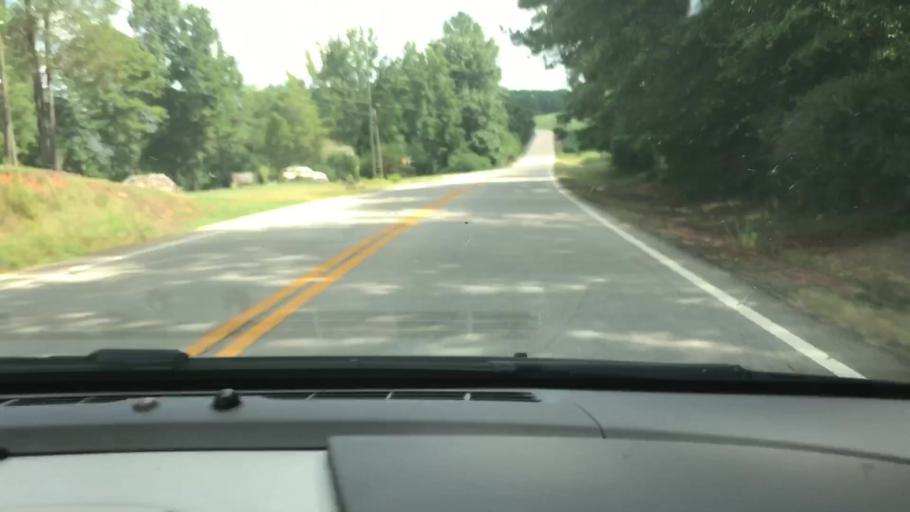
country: US
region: Georgia
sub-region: Troup County
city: La Grange
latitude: 32.9002
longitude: -85.0289
